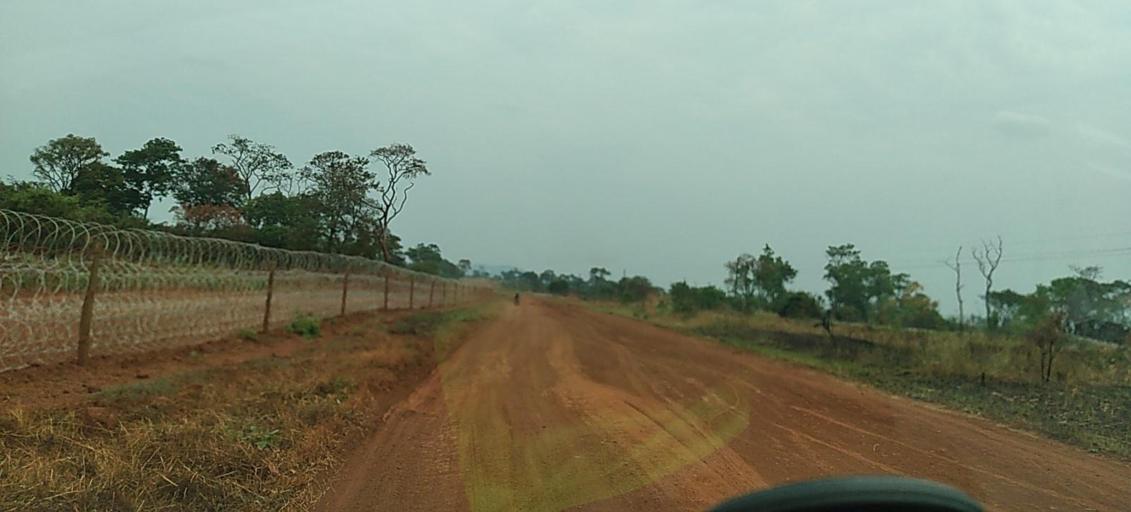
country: ZM
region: North-Western
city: Kansanshi
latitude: -12.0870
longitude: 26.4840
